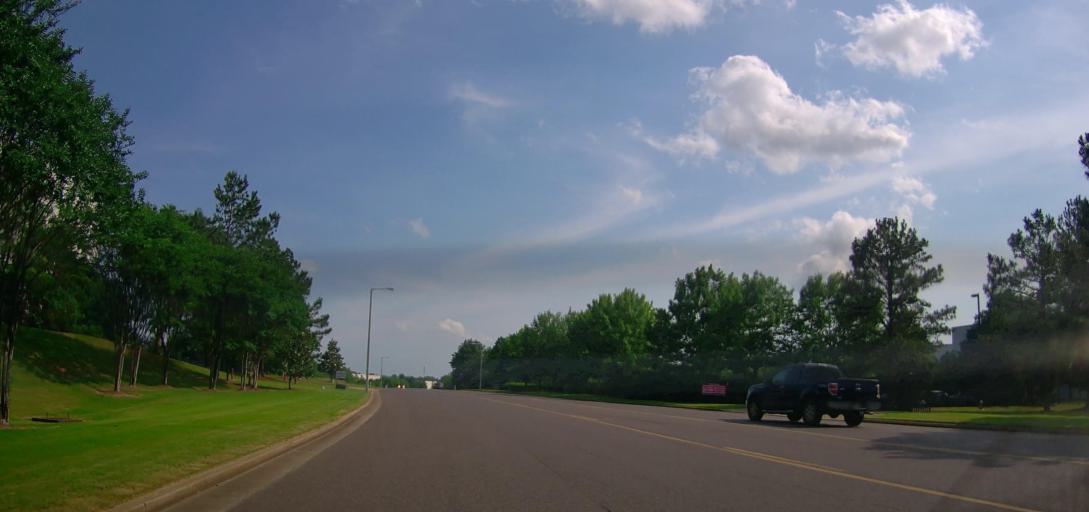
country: US
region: Mississippi
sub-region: De Soto County
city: Olive Branch
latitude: 35.0047
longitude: -89.8575
